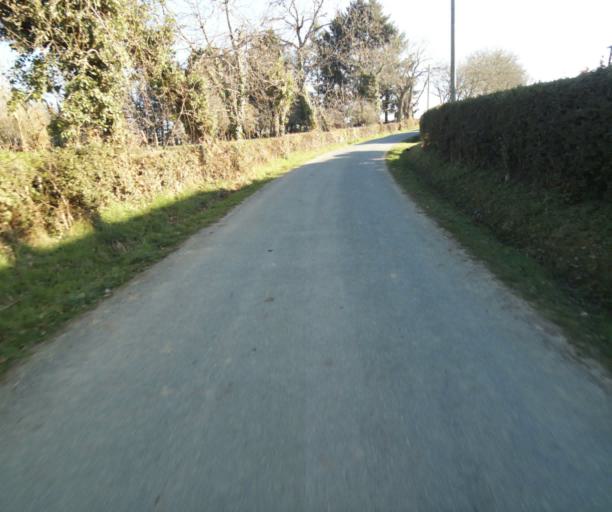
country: FR
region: Limousin
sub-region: Departement de la Correze
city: Seilhac
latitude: 45.3608
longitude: 1.7423
